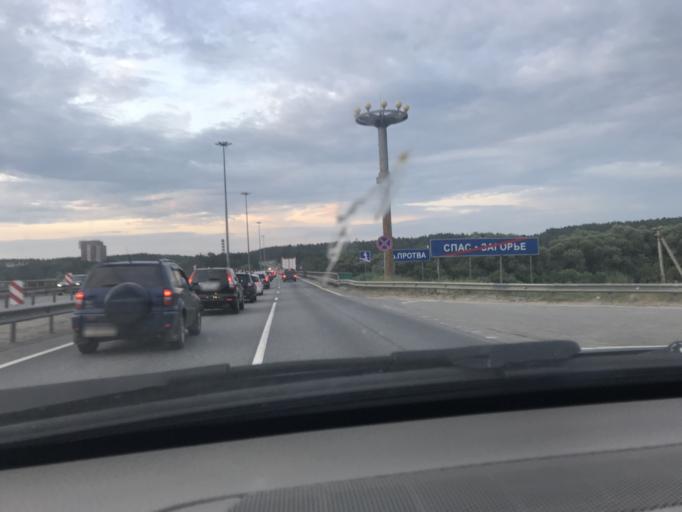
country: RU
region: Kaluga
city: Obninsk
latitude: 55.0486
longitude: 36.6072
